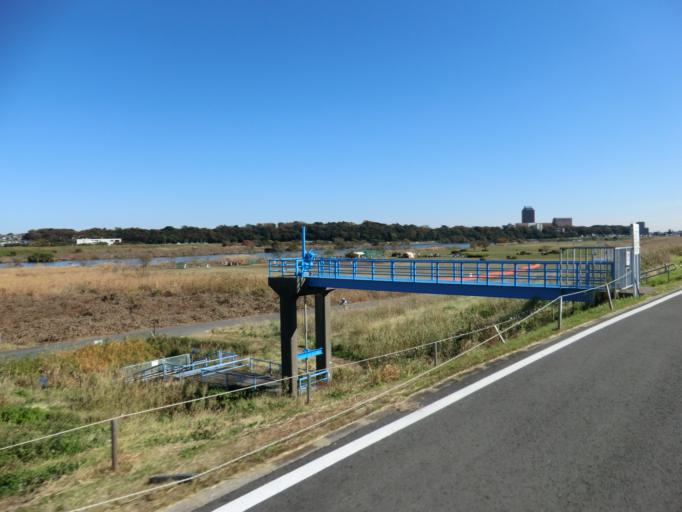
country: JP
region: Chiba
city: Matsudo
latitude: 35.7488
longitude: 139.8880
